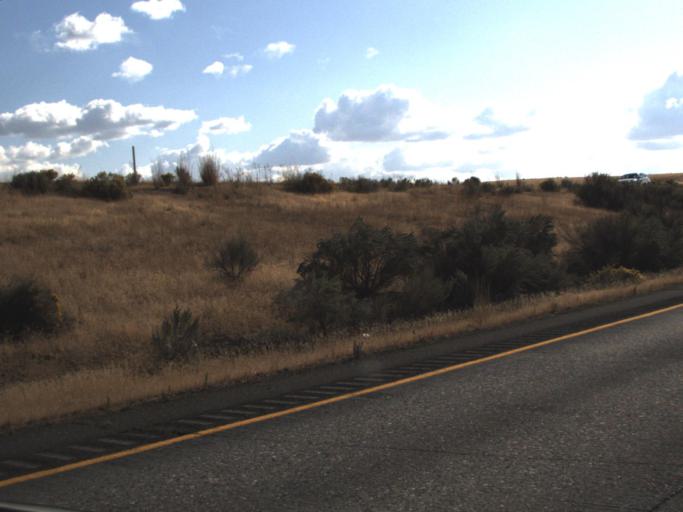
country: US
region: Oregon
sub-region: Umatilla County
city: Umatilla
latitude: 45.9787
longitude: -119.3297
